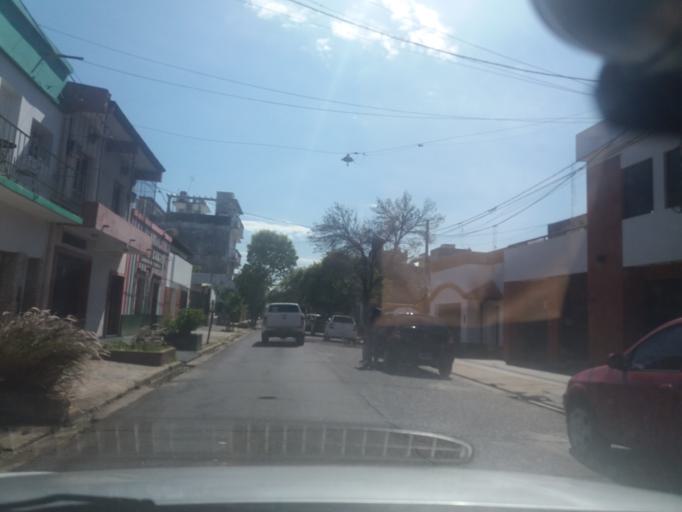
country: AR
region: Corrientes
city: Corrientes
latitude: -27.4731
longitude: -58.8460
